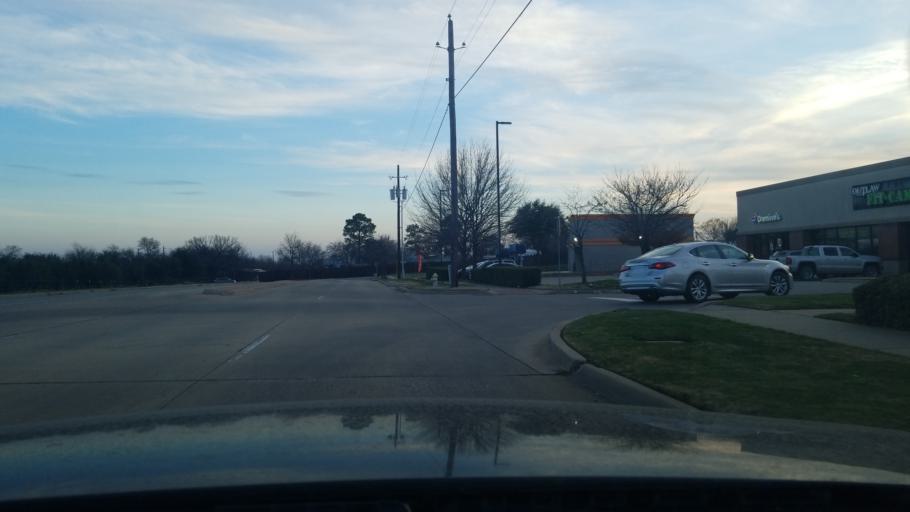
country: US
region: Texas
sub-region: Denton County
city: Hickory Creek
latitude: 33.1280
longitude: -97.0437
